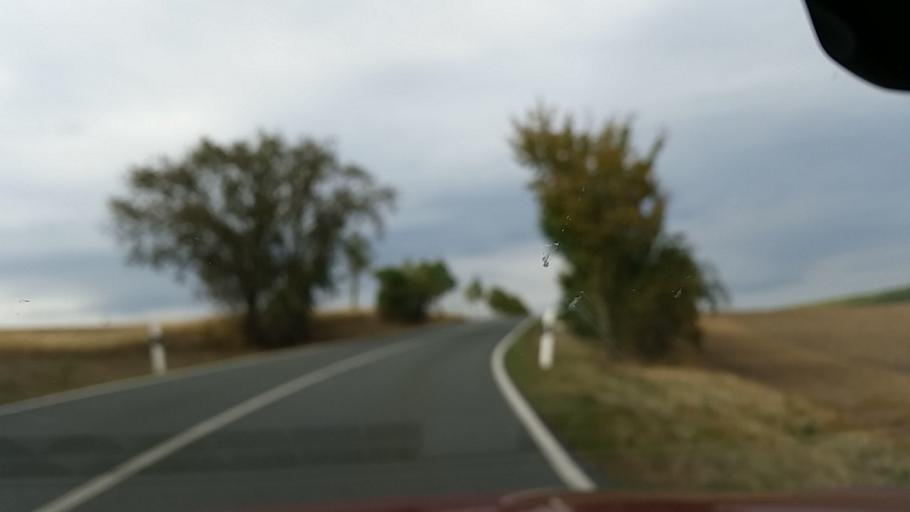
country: DE
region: Thuringia
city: Beichlingen
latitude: 51.2200
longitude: 11.2528
